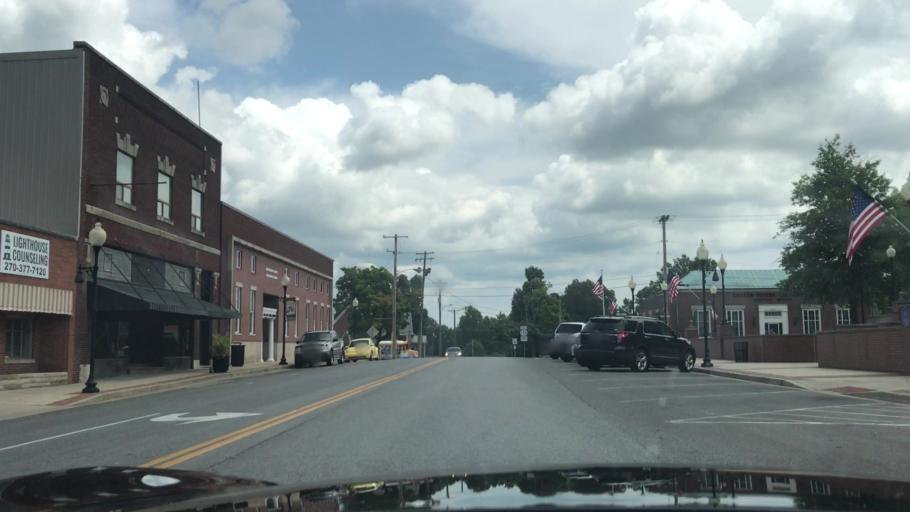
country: US
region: Kentucky
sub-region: Muhlenberg County
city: Greenville
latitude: 37.2010
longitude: -87.1783
